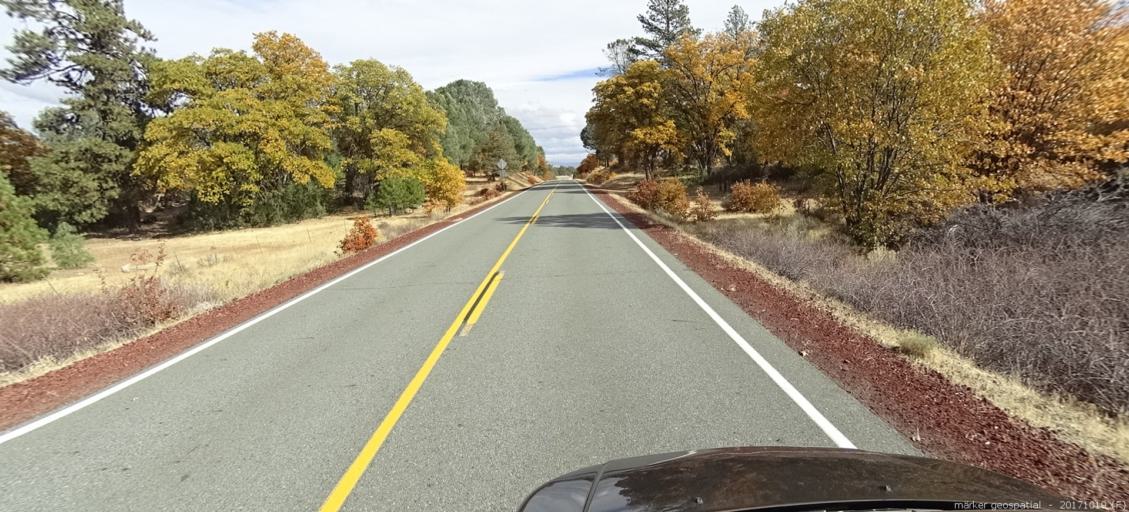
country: US
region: California
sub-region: Shasta County
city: Burney
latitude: 41.0089
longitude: -121.4650
